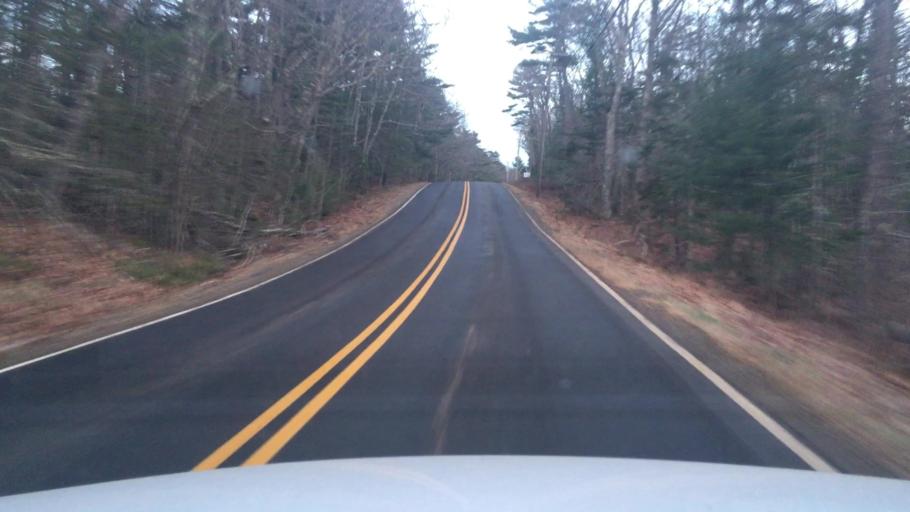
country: US
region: Maine
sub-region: Lincoln County
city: Bristol
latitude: 43.9114
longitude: -69.5278
